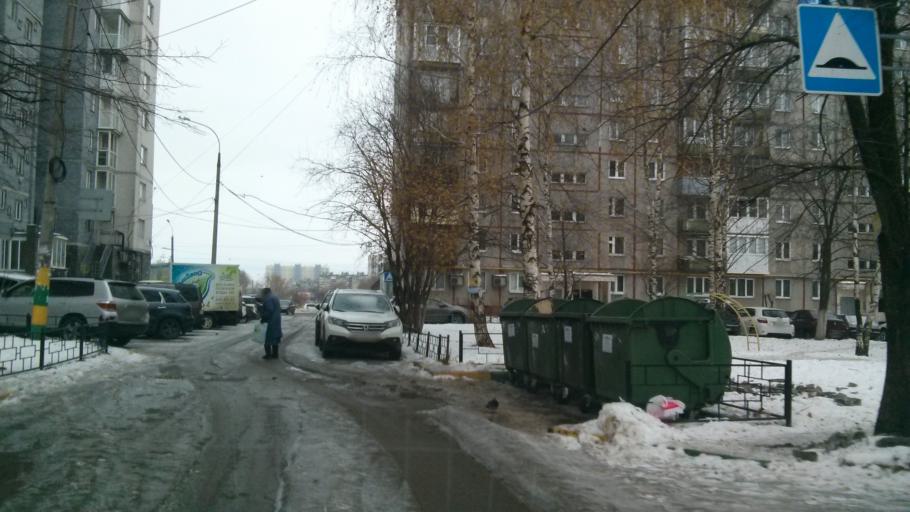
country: RU
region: Nizjnij Novgorod
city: Afonino
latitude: 56.2956
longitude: 44.0750
